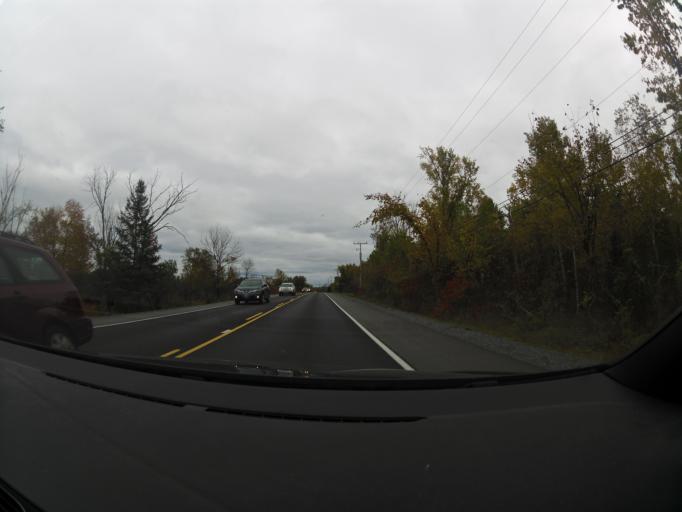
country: CA
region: Ontario
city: Bells Corners
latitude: 45.3979
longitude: -75.9907
